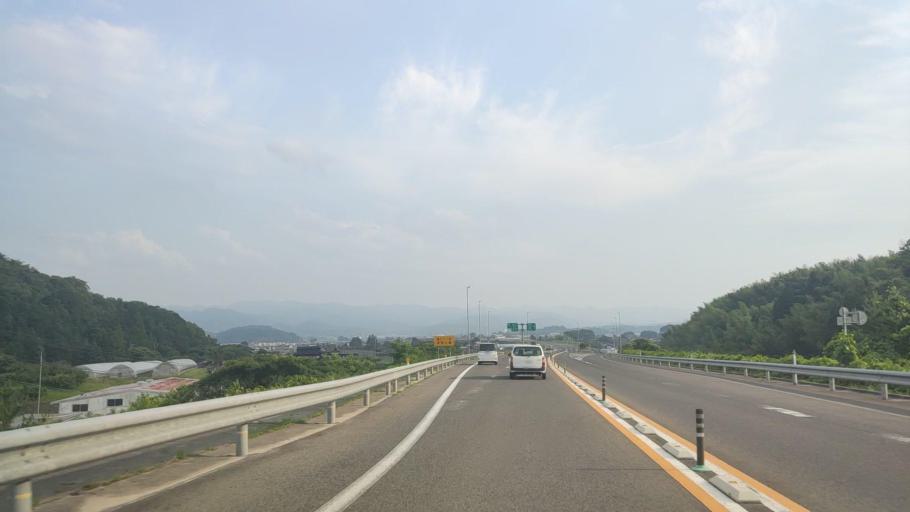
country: JP
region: Tottori
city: Kurayoshi
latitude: 35.4509
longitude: 133.8100
